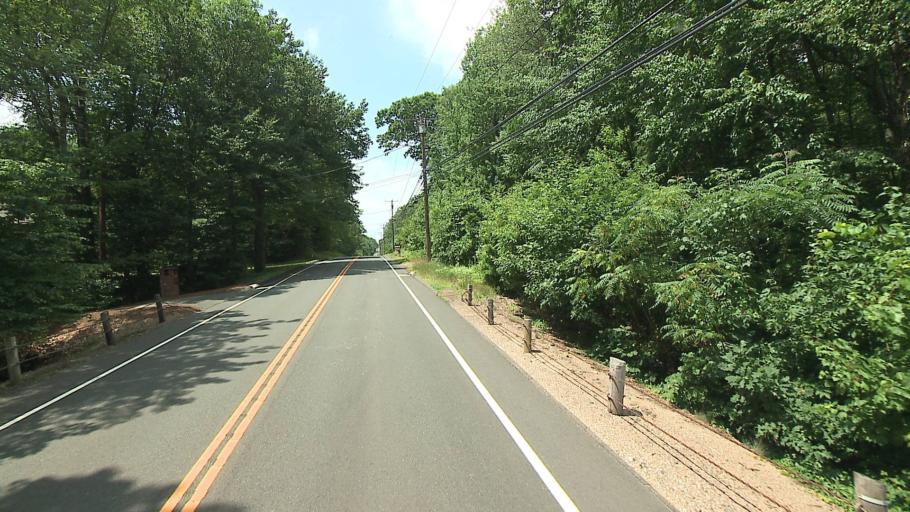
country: US
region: Connecticut
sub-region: Hartford County
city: North Granby
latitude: 41.9956
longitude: -72.8863
